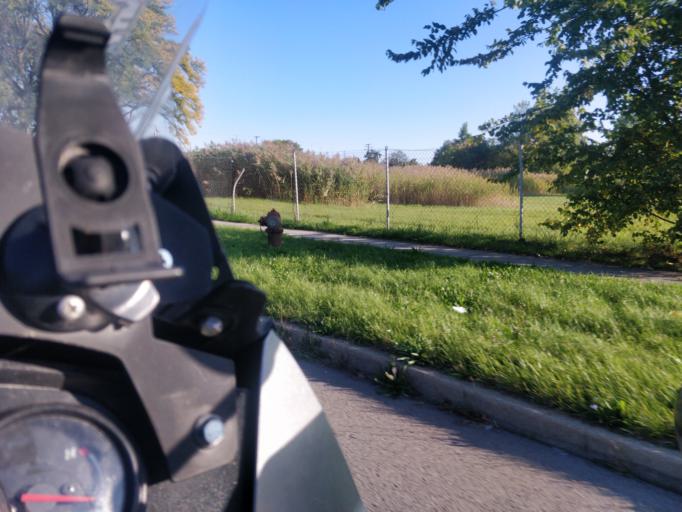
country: US
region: Michigan
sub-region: Wayne County
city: Lincoln Park
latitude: 42.2645
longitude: -83.1694
